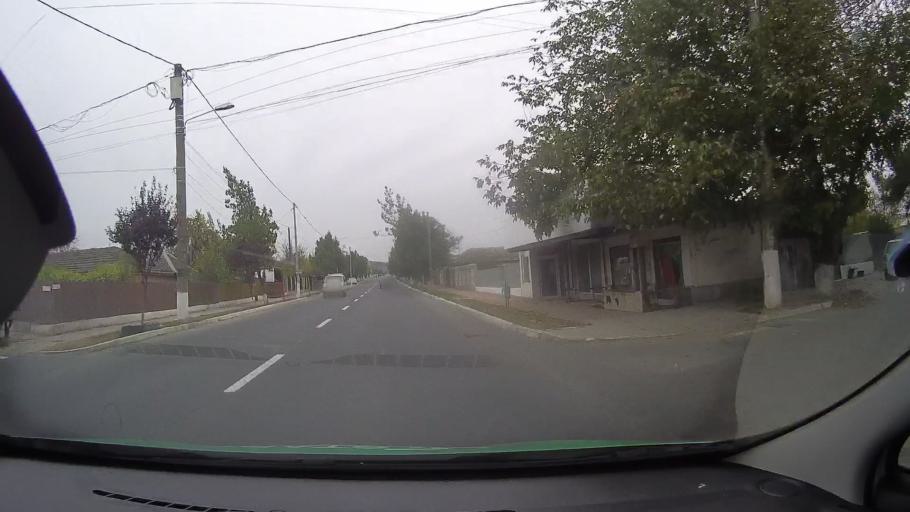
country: RO
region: Constanta
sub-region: Oras Harsova
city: Harsova
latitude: 44.6888
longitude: 27.9477
